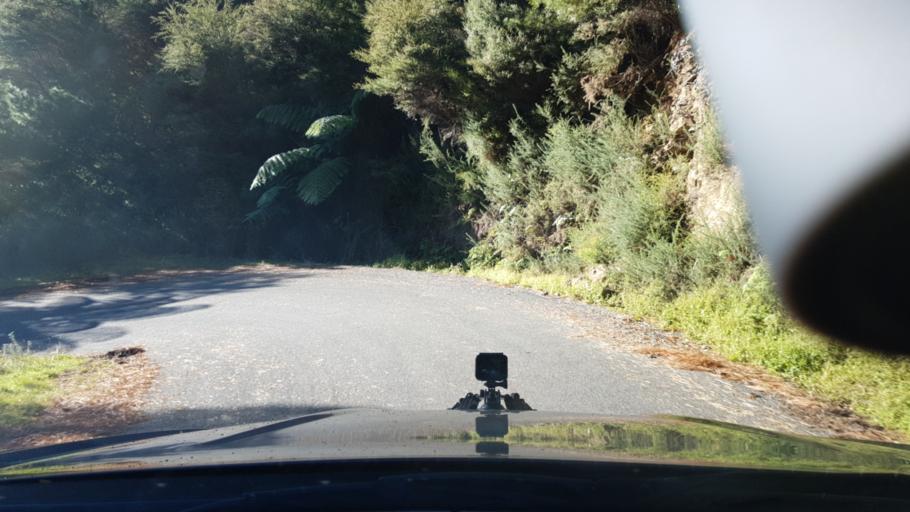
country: NZ
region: Marlborough
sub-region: Marlborough District
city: Picton
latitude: -41.1773
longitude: 173.9747
